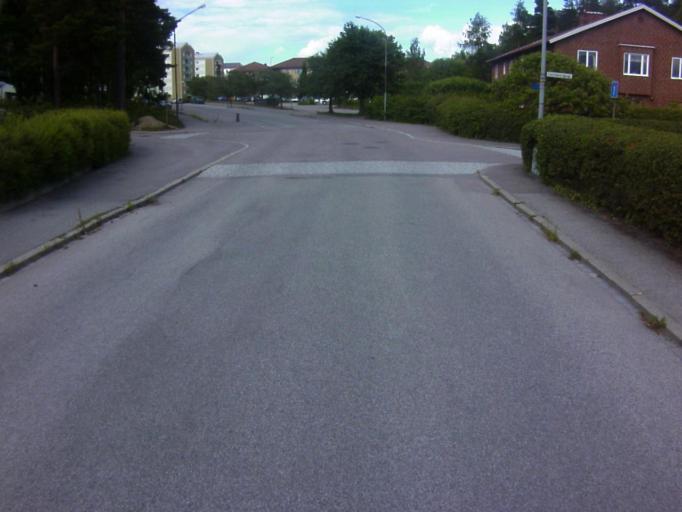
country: SE
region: Soedermanland
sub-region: Eskilstuna Kommun
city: Eskilstuna
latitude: 59.3577
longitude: 16.5116
